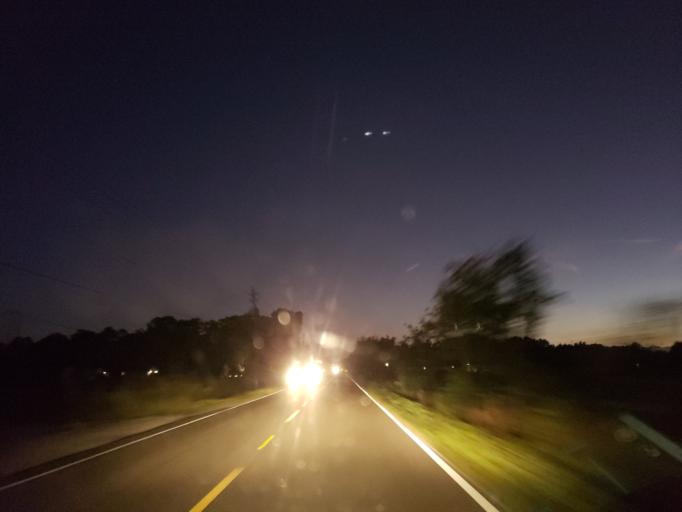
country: US
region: Florida
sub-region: Hillsborough County
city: Dover
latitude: 27.9888
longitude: -82.2197
